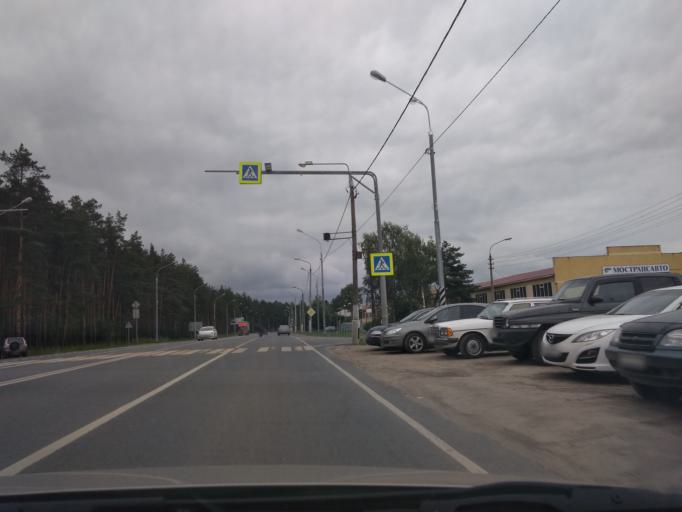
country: RU
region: Moskovskaya
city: Orekhovo-Zuyevo
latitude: 55.8283
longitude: 38.9636
